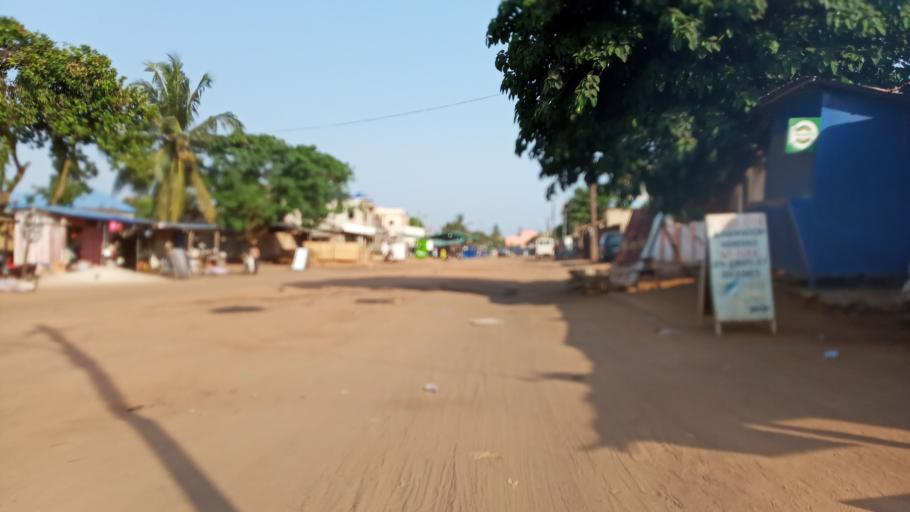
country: TG
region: Maritime
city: Lome
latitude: 6.1810
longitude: 1.1580
